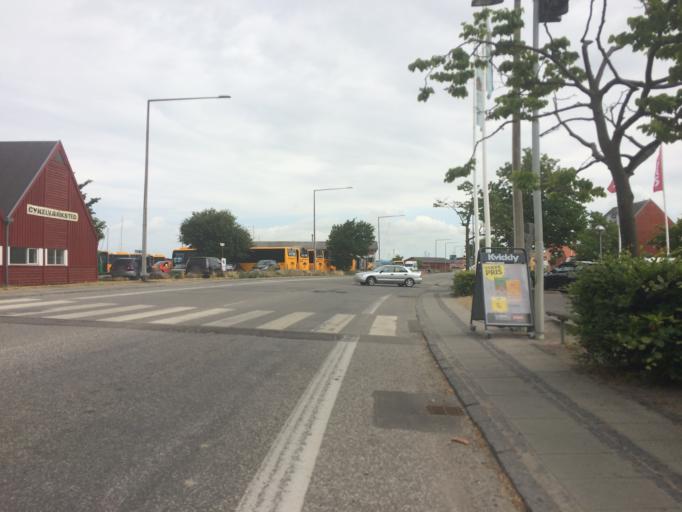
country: DK
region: Capital Region
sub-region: Bornholm Kommune
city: Ronne
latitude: 55.1018
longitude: 14.6917
